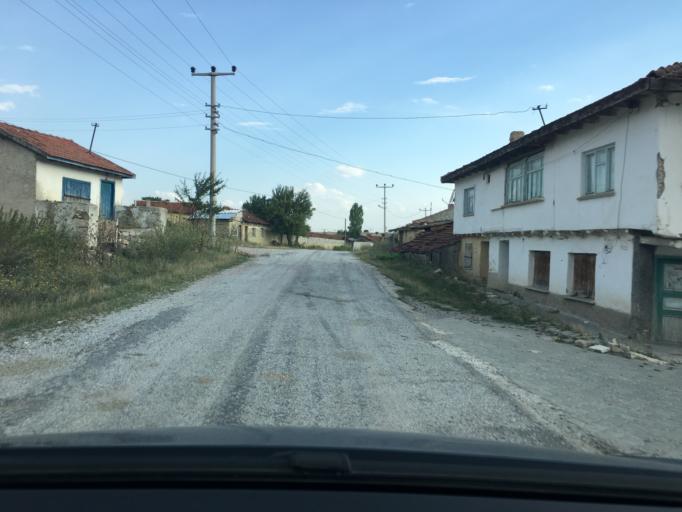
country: TR
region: Eskisehir
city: Kirka
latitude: 39.2754
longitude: 30.6768
